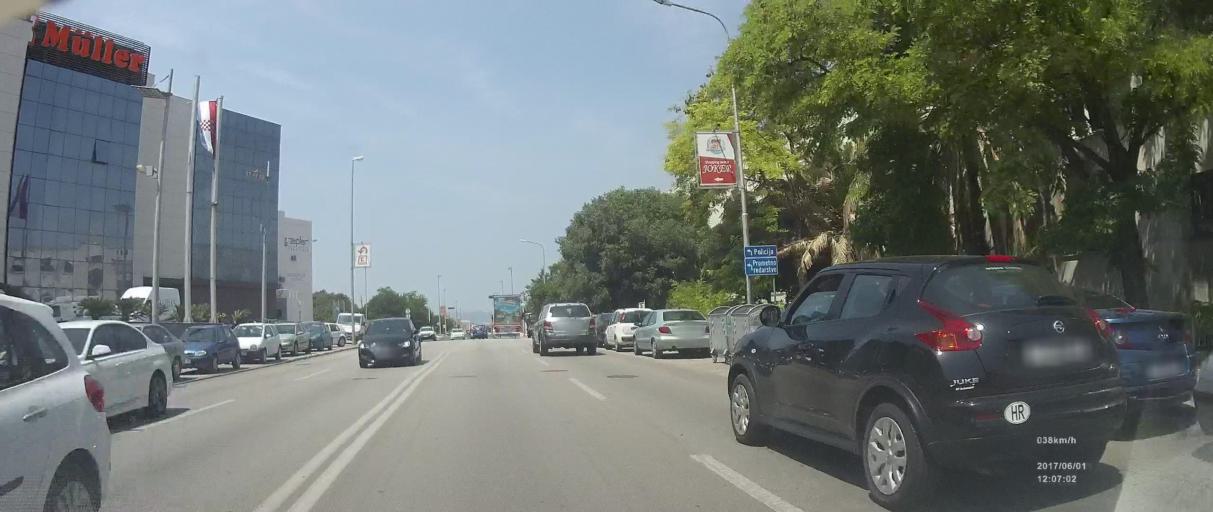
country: HR
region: Splitsko-Dalmatinska
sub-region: Grad Split
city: Split
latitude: 43.5208
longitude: 16.4472
